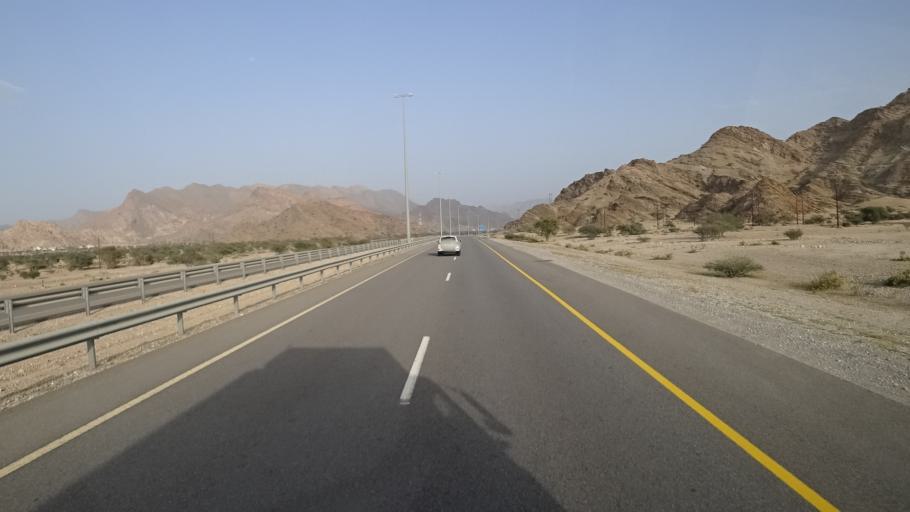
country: OM
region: Muhafazat Masqat
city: Muscat
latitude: 23.3639
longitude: 58.6600
